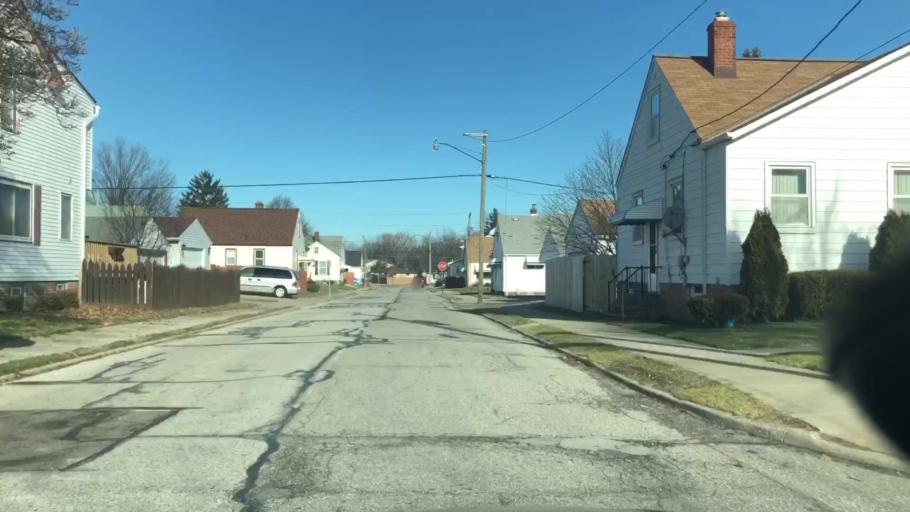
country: US
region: Ohio
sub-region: Cuyahoga County
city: Brooklyn
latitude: 41.4271
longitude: -81.7305
